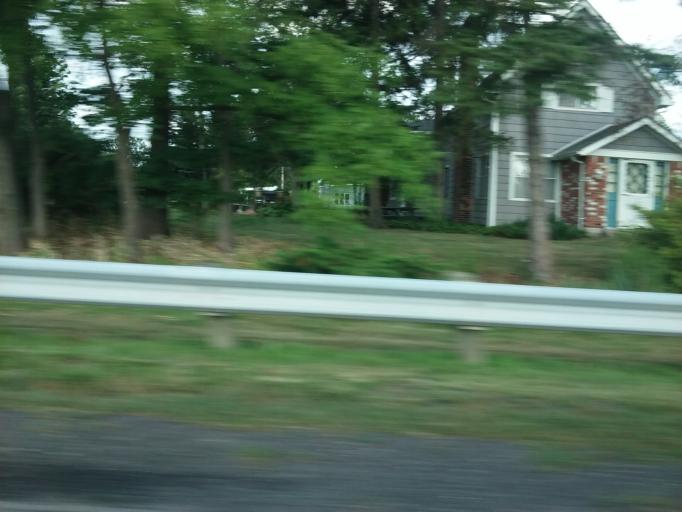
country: US
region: Ohio
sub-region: Wood County
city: Bowling Green
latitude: 41.2981
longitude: -83.6503
